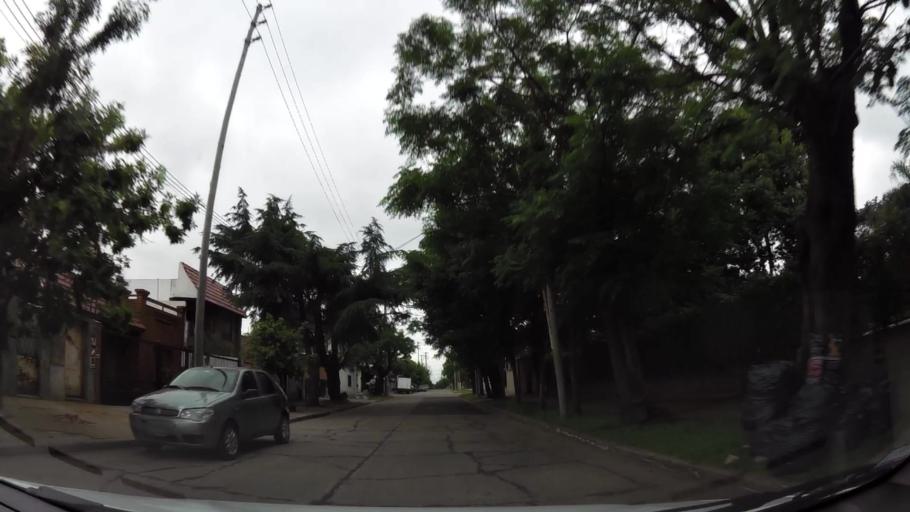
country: AR
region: Buenos Aires F.D.
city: Villa Lugano
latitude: -34.7067
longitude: -58.5124
